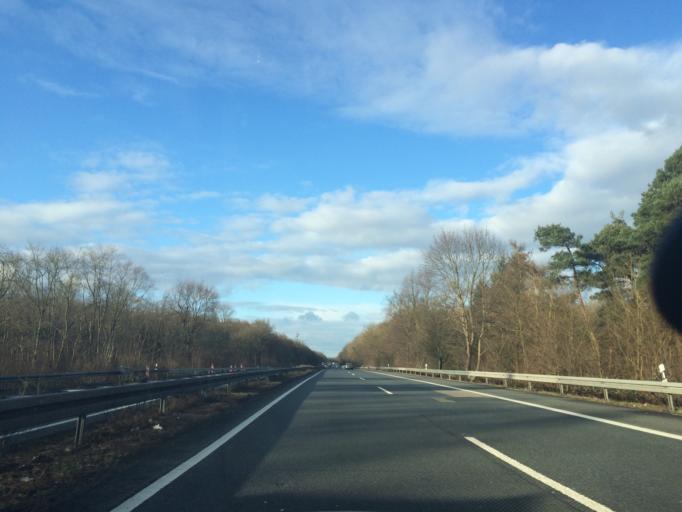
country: DE
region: Hesse
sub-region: Regierungsbezirk Darmstadt
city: Einhausen
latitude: 49.7025
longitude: 8.5482
